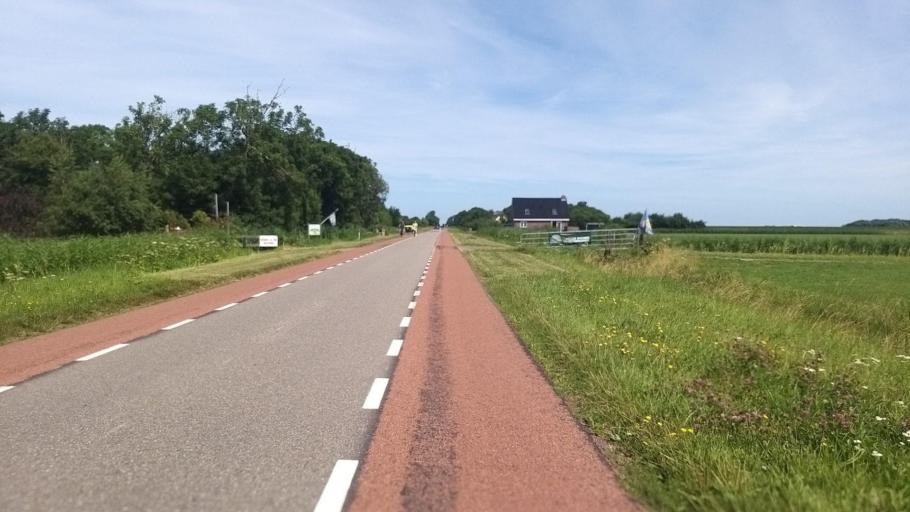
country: NL
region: North Holland
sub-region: Gemeente Texel
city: Den Burg
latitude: 53.1203
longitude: 4.8531
